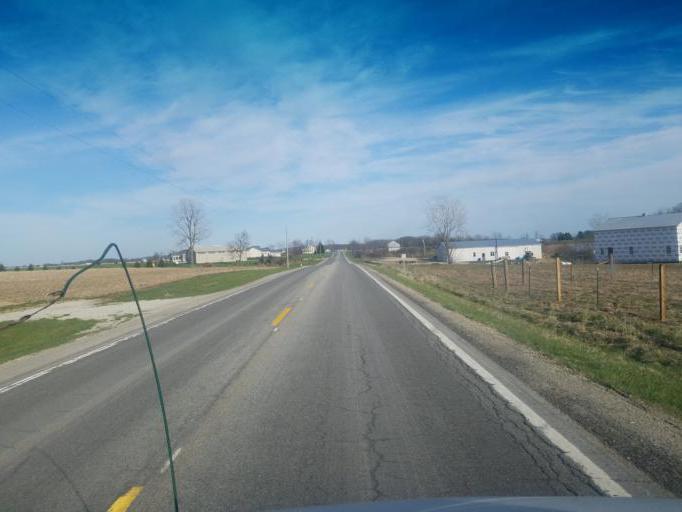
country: US
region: Ohio
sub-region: Shelby County
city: Jackson Center
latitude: 40.3388
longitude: -84.0249
